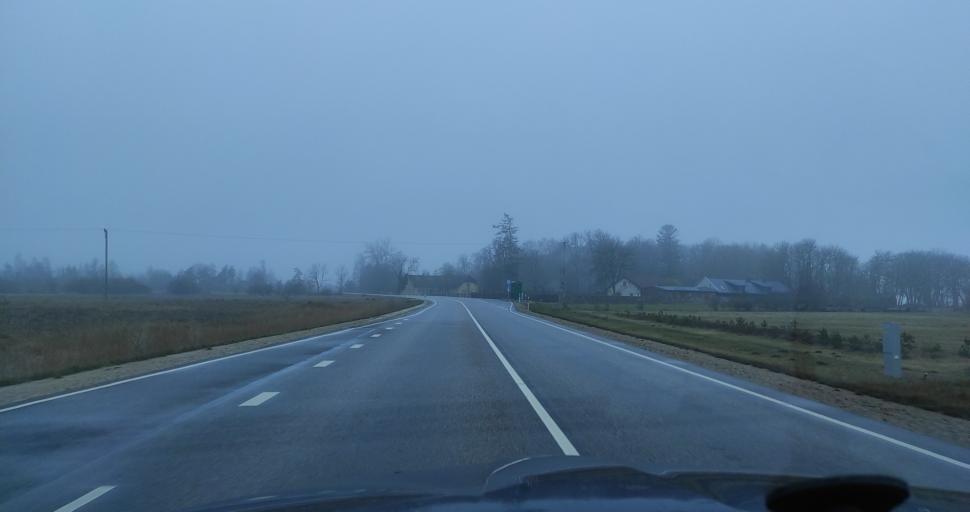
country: LV
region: Pavilostas
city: Pavilosta
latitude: 56.9376
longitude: 21.2782
